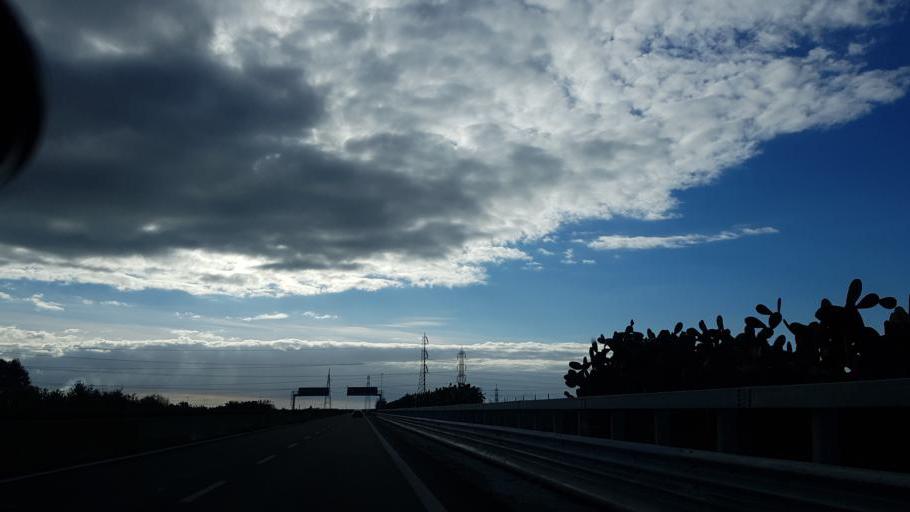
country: IT
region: Apulia
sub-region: Provincia di Brindisi
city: La Rosa
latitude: 40.6107
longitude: 17.9609
